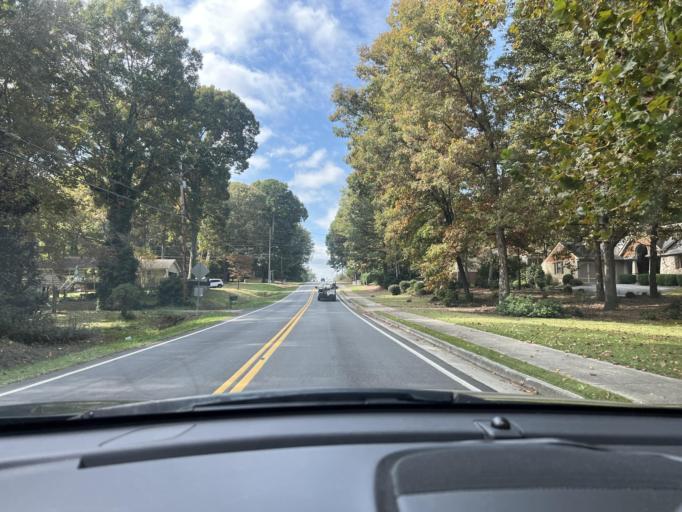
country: US
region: Georgia
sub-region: Gwinnett County
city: Snellville
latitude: 33.8820
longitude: -84.0036
